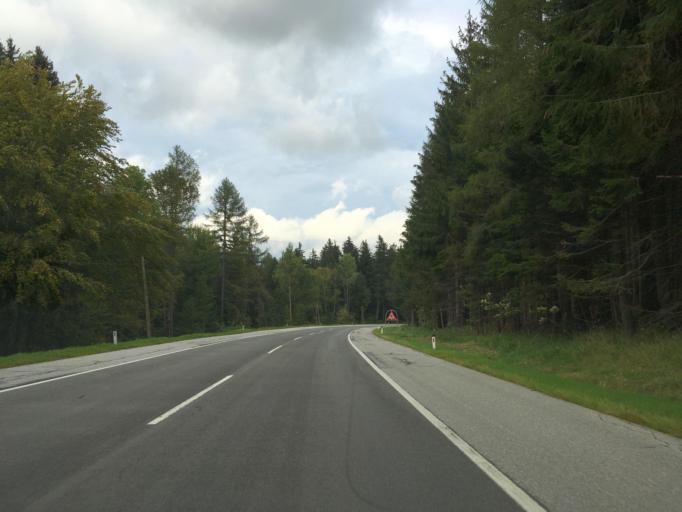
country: AT
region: Lower Austria
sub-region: Politischer Bezirk Neunkirchen
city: Monichkirchen
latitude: 47.5177
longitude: 16.0556
